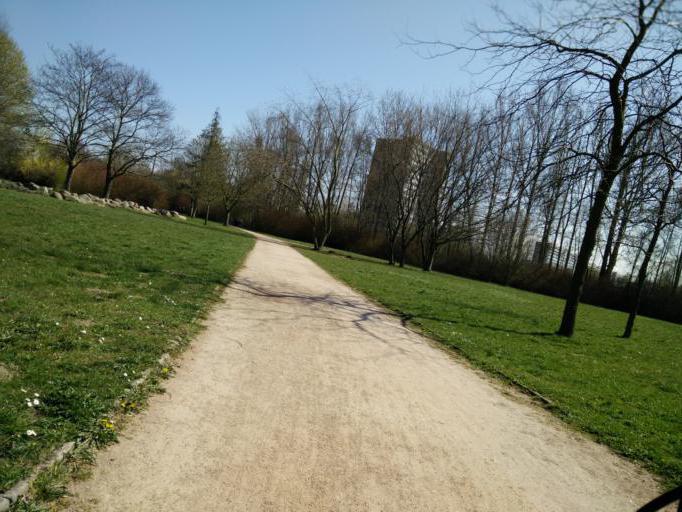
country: DE
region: Mecklenburg-Vorpommern
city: Lambrechtshagen
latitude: 54.1291
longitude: 12.0541
